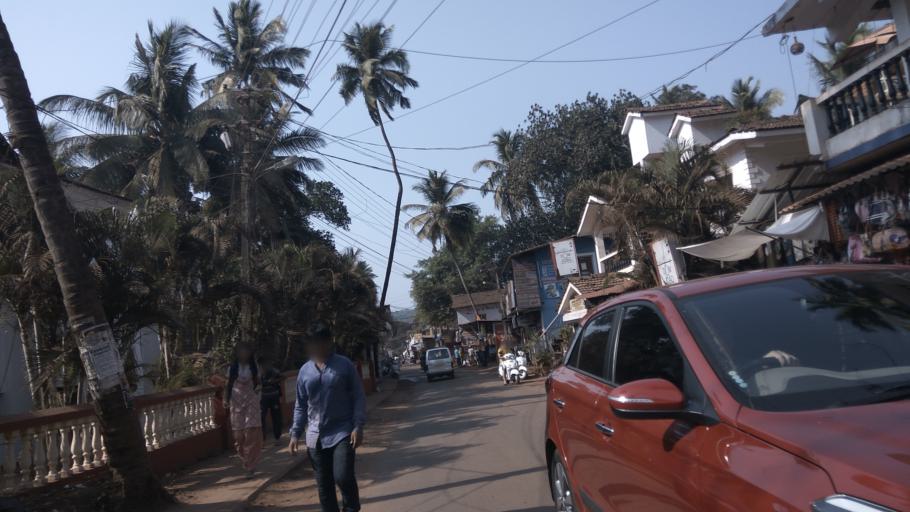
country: IN
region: Goa
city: Calangute
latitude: 15.5595
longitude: 73.7540
